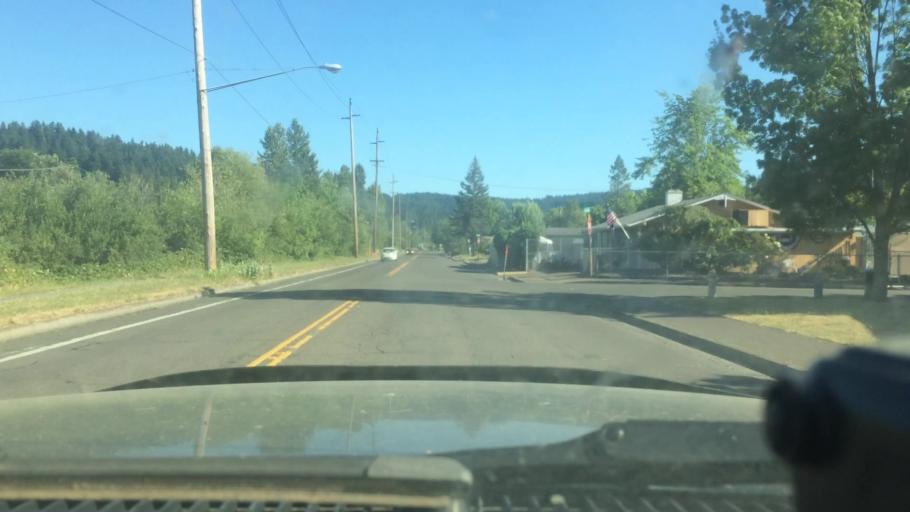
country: US
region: Oregon
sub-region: Lane County
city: Eugene
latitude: 44.0168
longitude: -123.0794
